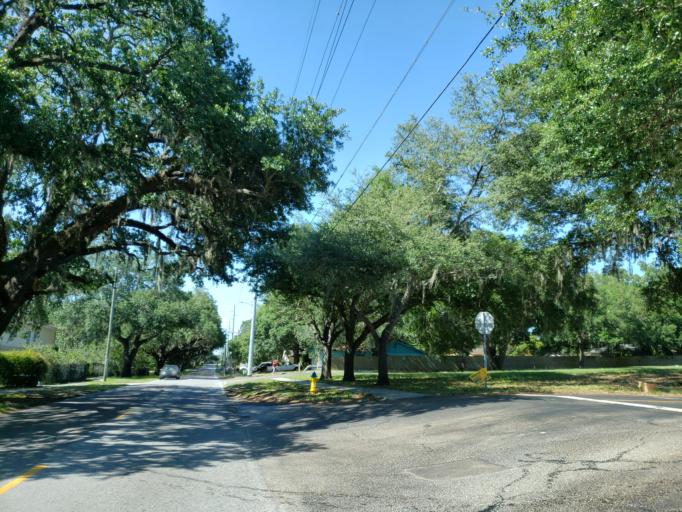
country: US
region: Florida
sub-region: Hillsborough County
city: Mango
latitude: 27.9829
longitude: -82.3105
